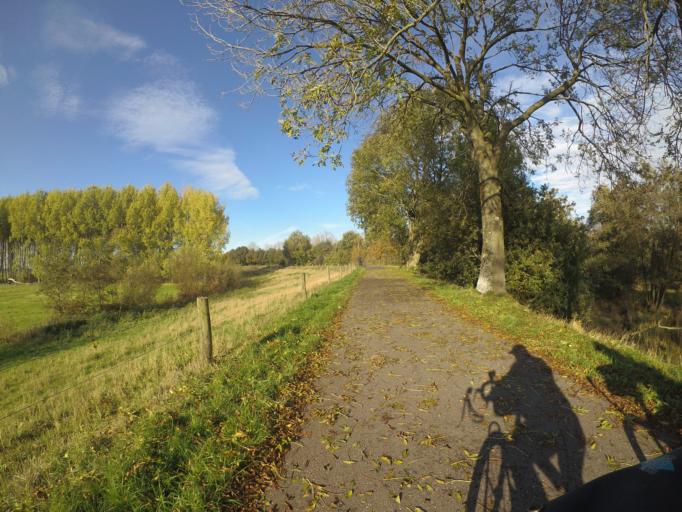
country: NL
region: North Brabant
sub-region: Gemeente Heusden
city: Heusden
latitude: 51.7096
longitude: 5.1109
